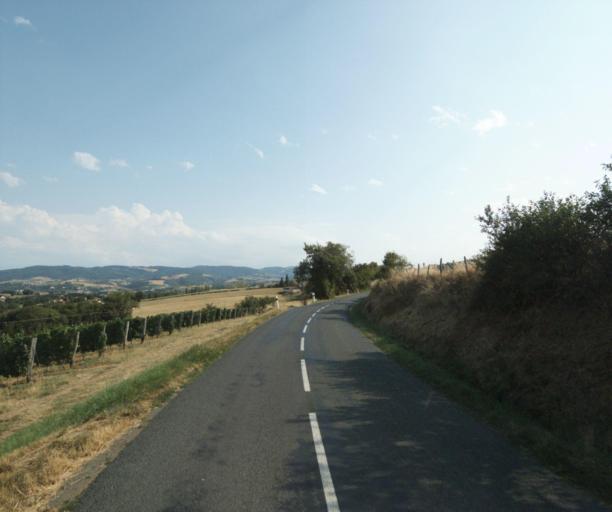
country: FR
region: Rhone-Alpes
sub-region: Departement du Rhone
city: Savigny
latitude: 45.8324
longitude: 4.5704
